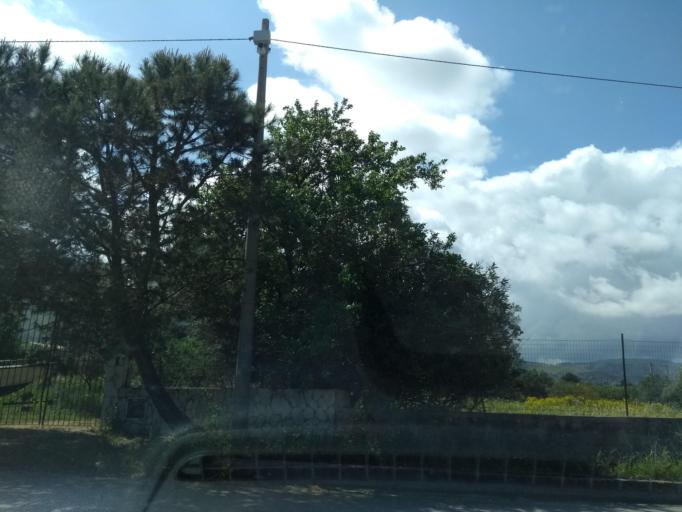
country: IT
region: Sicily
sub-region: Trapani
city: Castellammare del Golfo
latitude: 38.0445
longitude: 12.8494
